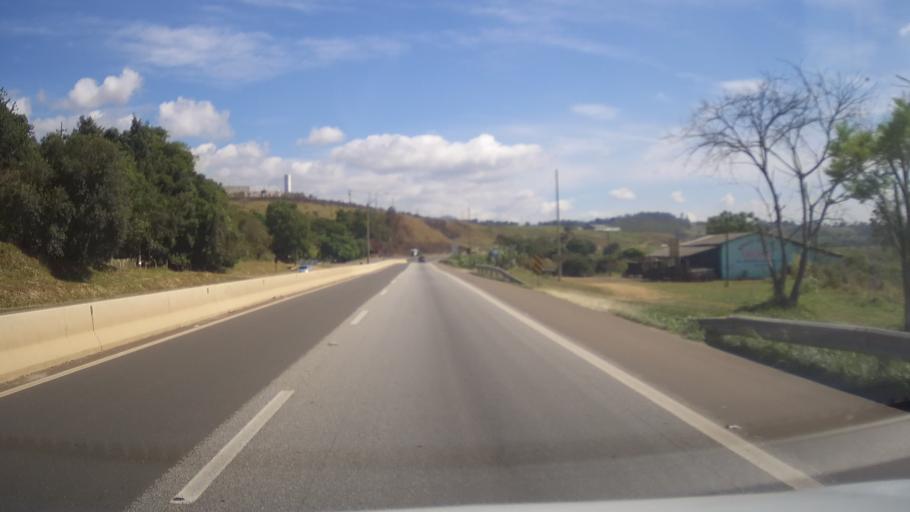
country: BR
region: Minas Gerais
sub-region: Cambui
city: Cambui
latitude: -22.5512
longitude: -46.0394
